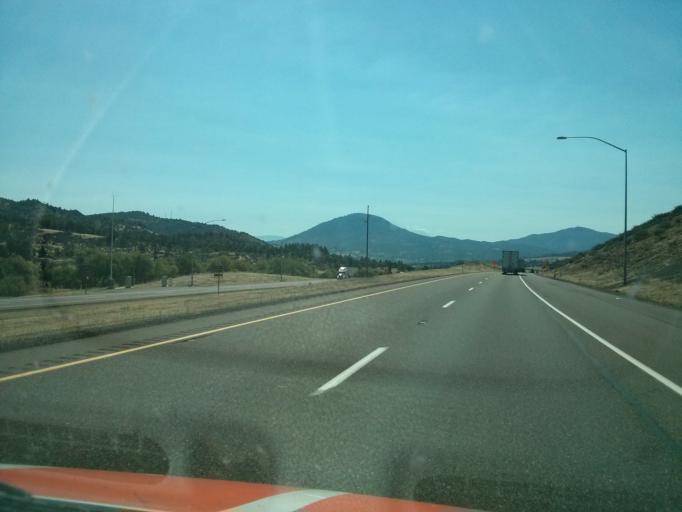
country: US
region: California
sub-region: Siskiyou County
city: Yreka
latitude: 41.9502
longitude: -122.5899
